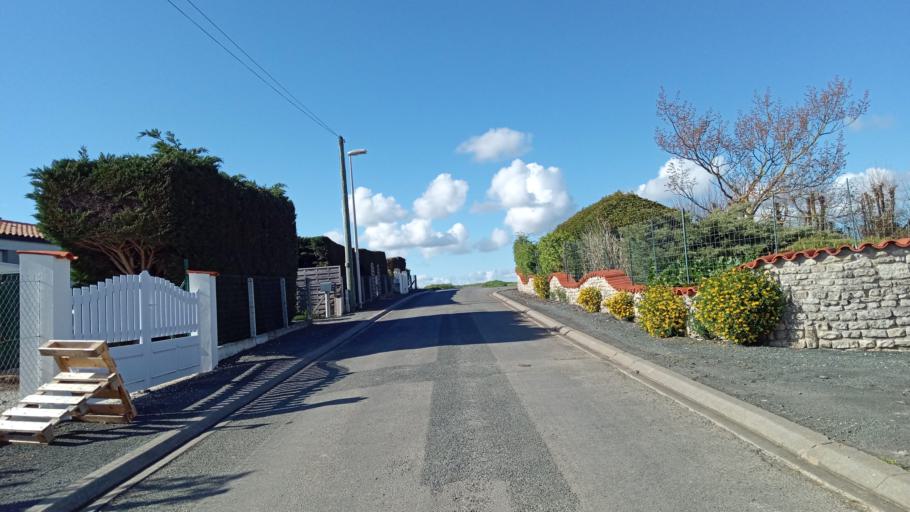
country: FR
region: Poitou-Charentes
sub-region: Departement de la Charente-Maritime
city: Verines
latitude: 46.1548
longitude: -0.9334
